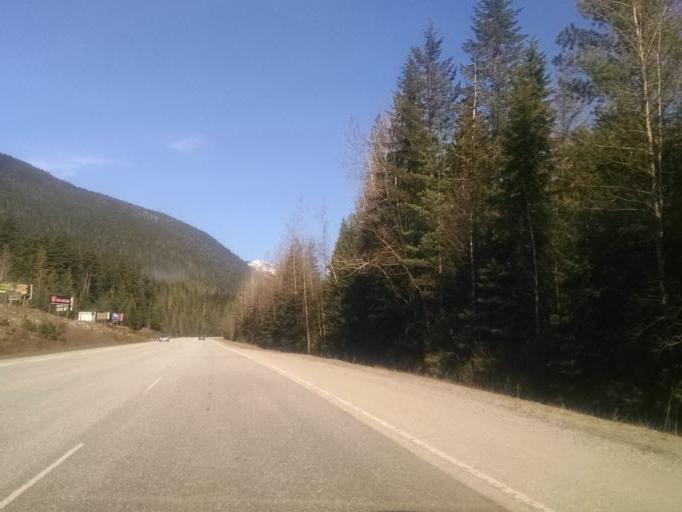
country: CA
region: British Columbia
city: Revelstoke
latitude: 51.0138
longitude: -118.0885
